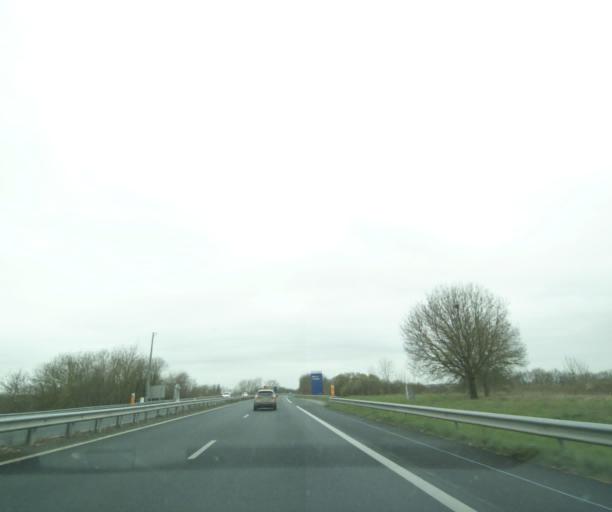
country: FR
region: Poitou-Charentes
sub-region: Departement de la Charente-Maritime
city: Breuil-Magne
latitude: 45.9667
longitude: -0.9768
